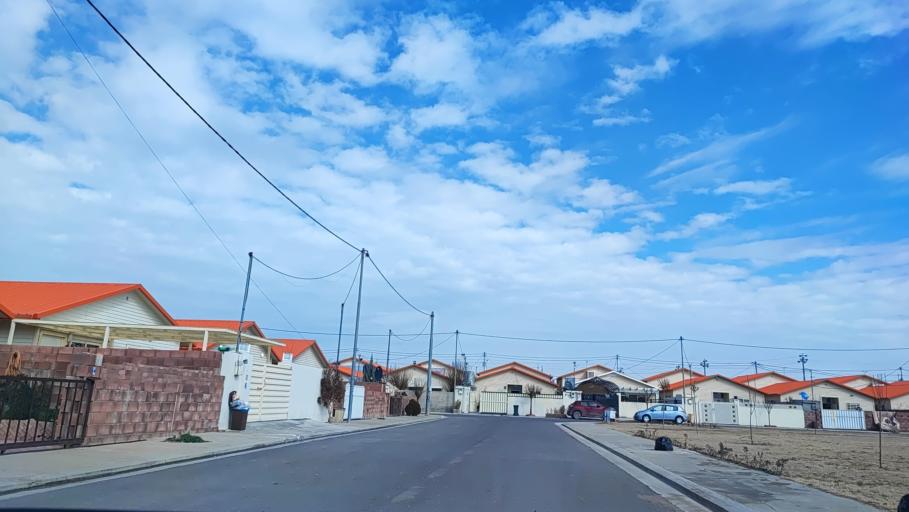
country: IQ
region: Arbil
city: Erbil
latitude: 36.2840
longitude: 44.0691
